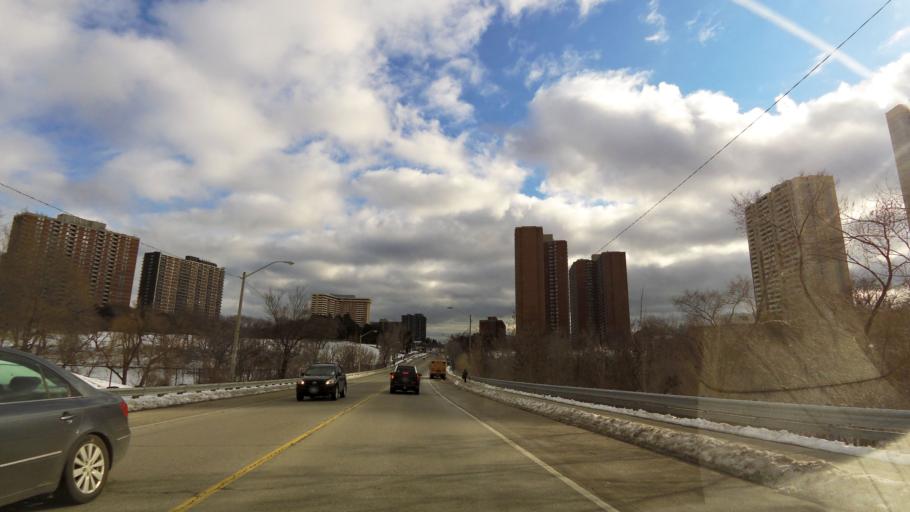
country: CA
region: Ontario
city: Scarborough
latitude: 43.6988
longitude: -79.2916
